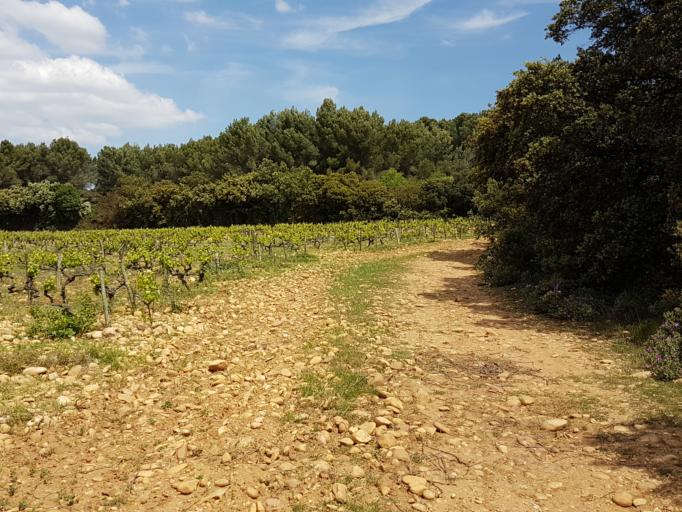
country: FR
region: Provence-Alpes-Cote d'Azur
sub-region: Departement du Vaucluse
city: Bedarrides
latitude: 44.0419
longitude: 4.8675
